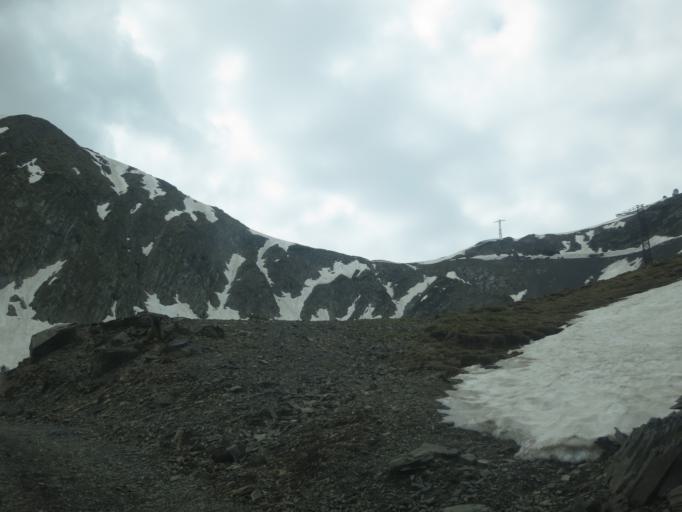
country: GE
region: Kakheti
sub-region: Telavi
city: Telavi
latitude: 42.2841
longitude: 45.5087
